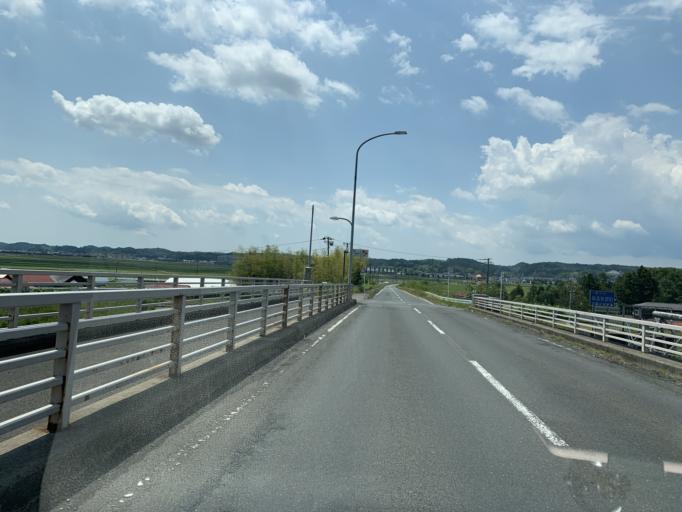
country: JP
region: Miyagi
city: Kogota
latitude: 38.5271
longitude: 141.0580
